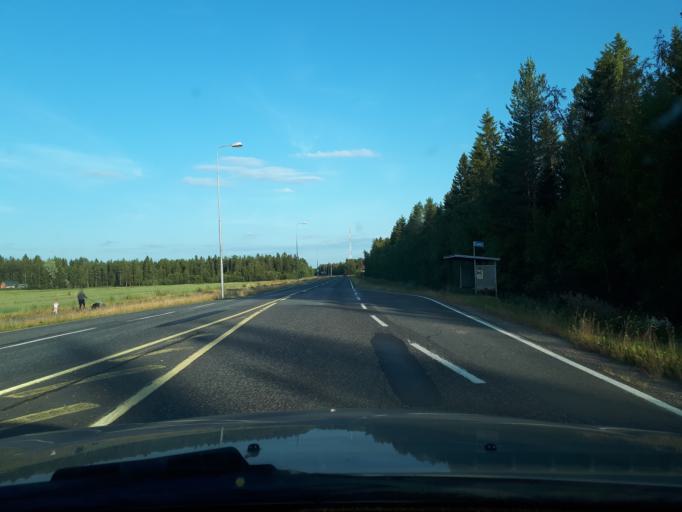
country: FI
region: Northern Ostrobothnia
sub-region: Oulu
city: Oulunsalo
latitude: 64.9788
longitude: 25.2771
